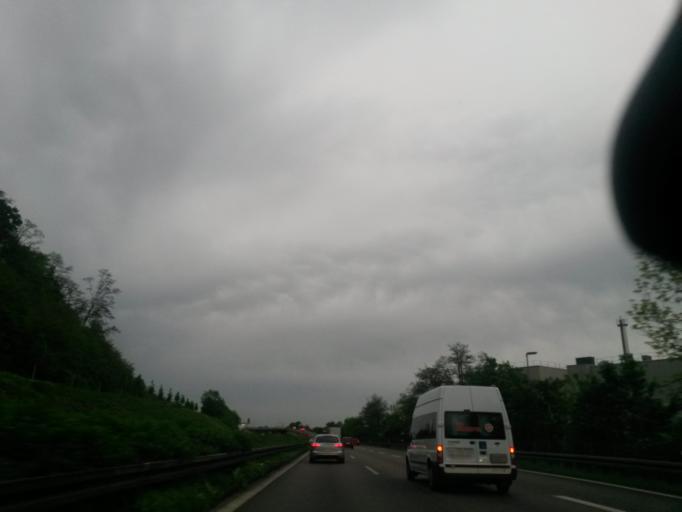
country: DE
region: Baden-Wuerttemberg
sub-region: Regierungsbezirk Stuttgart
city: Ostfildern
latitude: 48.7472
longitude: 9.2656
